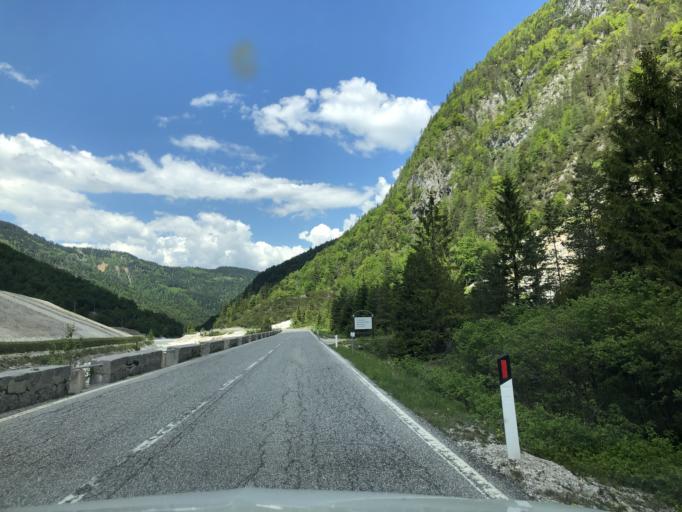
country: IT
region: Friuli Venezia Giulia
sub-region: Provincia di Udine
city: Tarvisio
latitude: 46.4534
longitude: 13.5754
